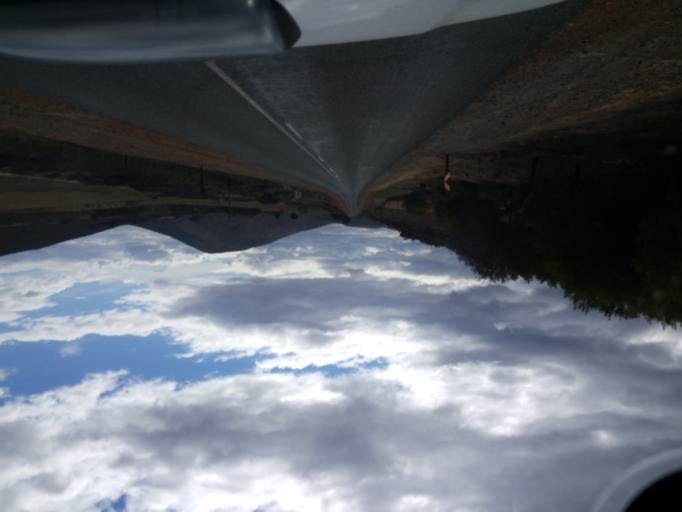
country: ZA
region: Western Cape
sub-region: Eden District Municipality
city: George
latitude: -33.8203
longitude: 22.3754
